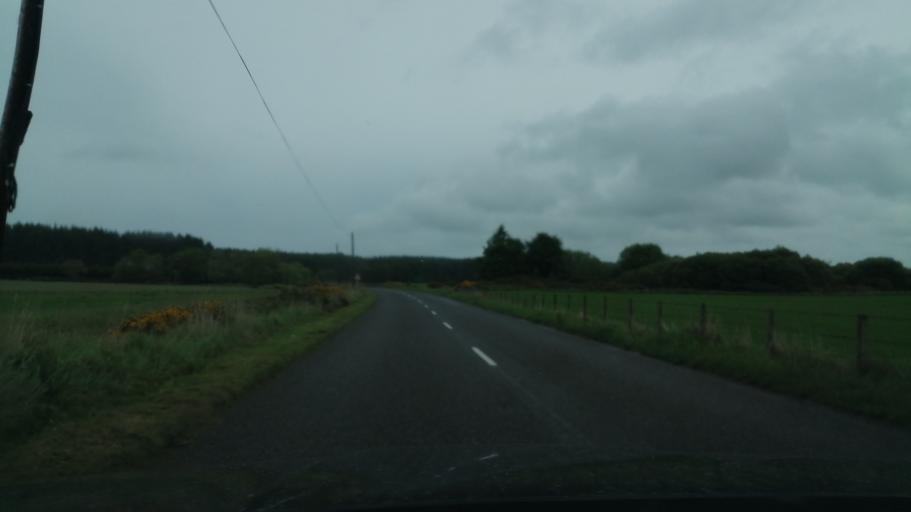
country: GB
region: Scotland
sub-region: Aberdeenshire
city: Portsoy
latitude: 57.6183
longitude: -2.7220
